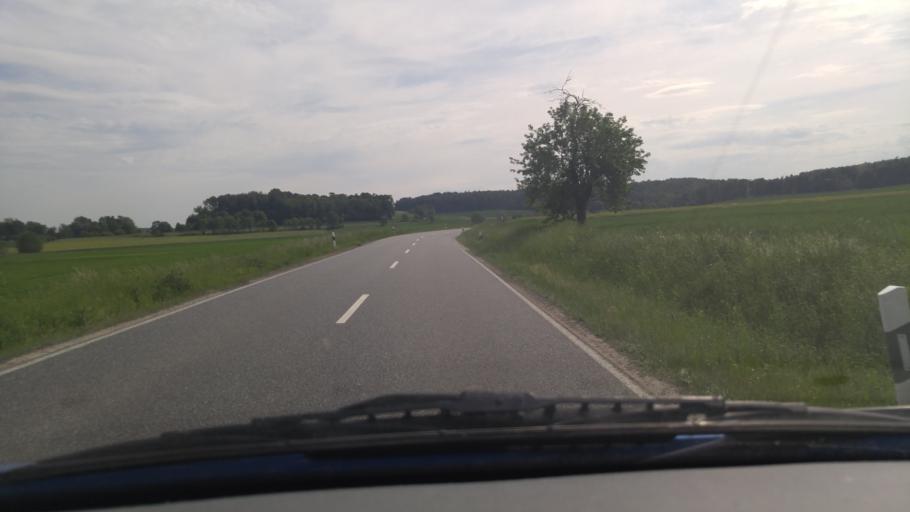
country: DE
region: Hesse
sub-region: Regierungsbezirk Darmstadt
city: Nidda
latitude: 50.4255
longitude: 8.9697
